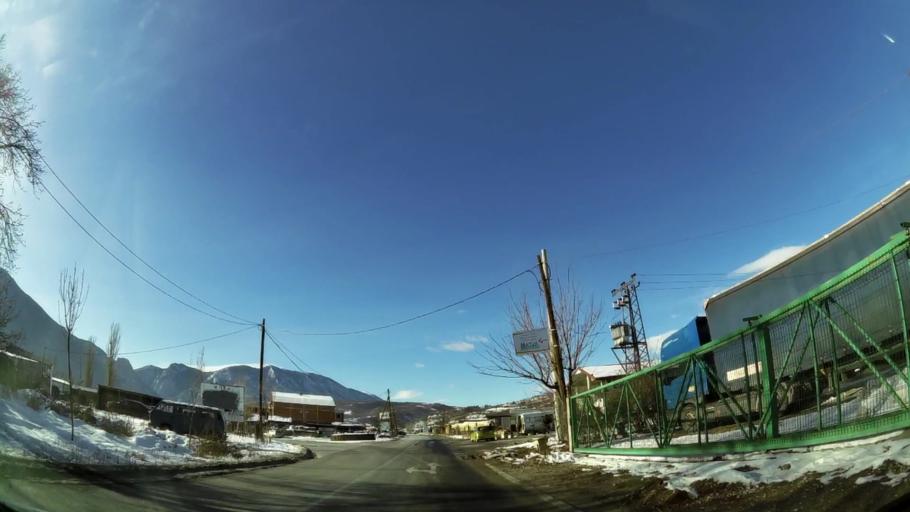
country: MK
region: Saraj
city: Saraj
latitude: 41.9931
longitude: 21.3185
